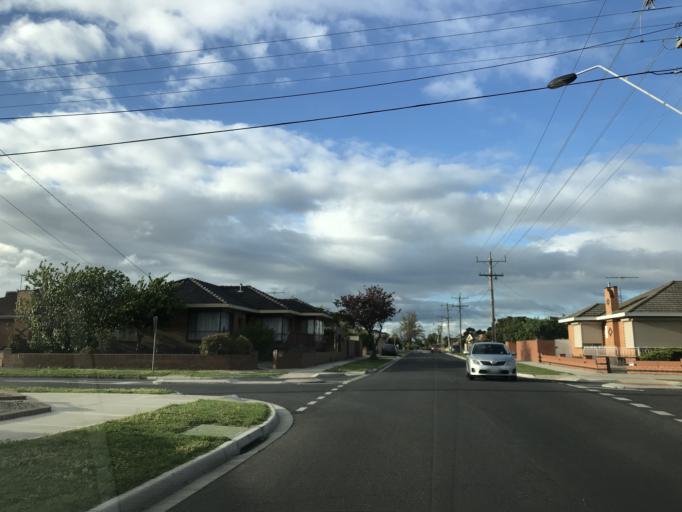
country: AU
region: Victoria
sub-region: Brimbank
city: Sunshine West
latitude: -37.7920
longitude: 144.8049
